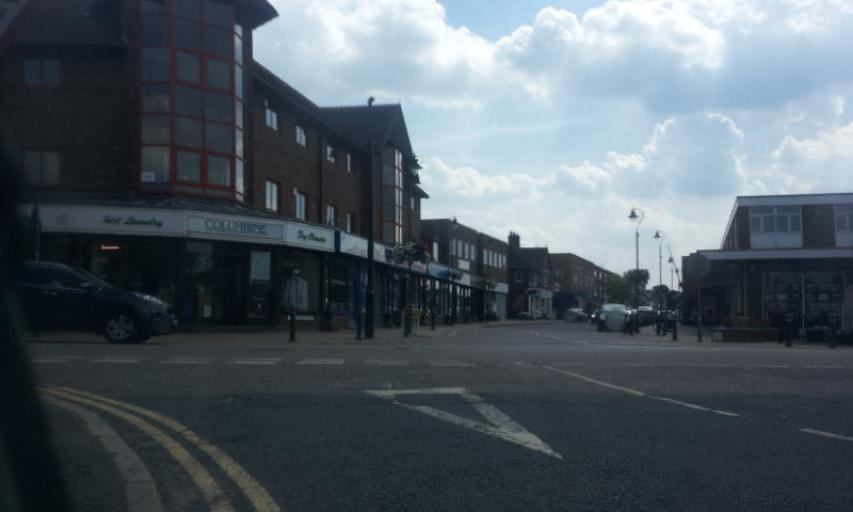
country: GB
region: England
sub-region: Kent
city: Paddock Wood
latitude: 51.1816
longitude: 0.3892
